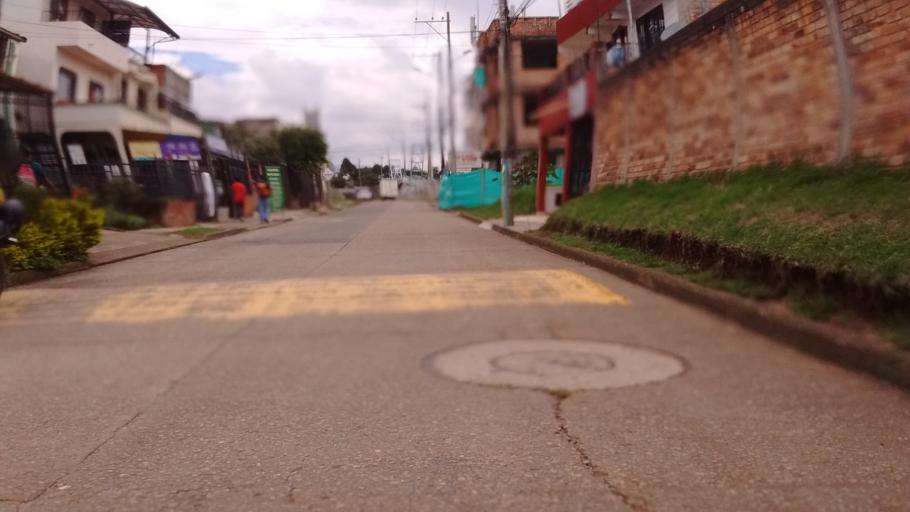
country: CO
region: Cauca
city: Popayan
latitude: 2.4797
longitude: -76.5776
